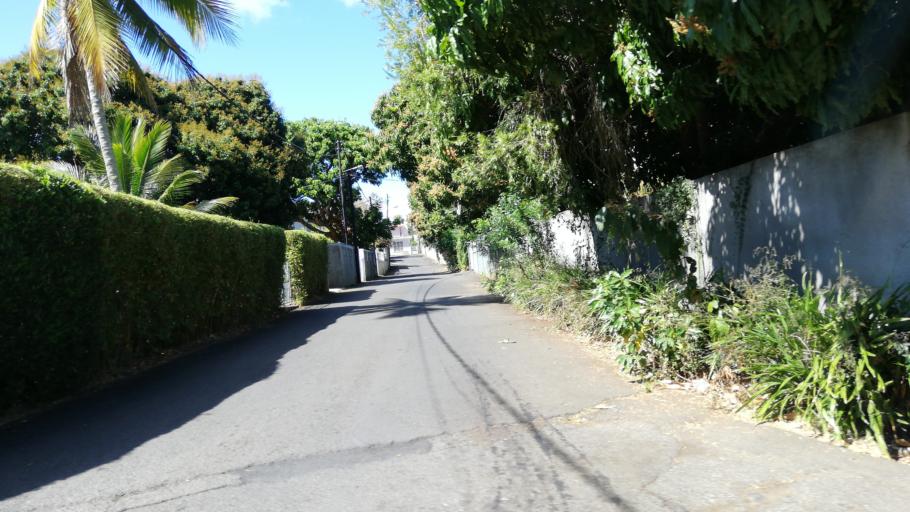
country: MU
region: Plaines Wilhems
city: Ebene
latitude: -20.2352
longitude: 57.4754
